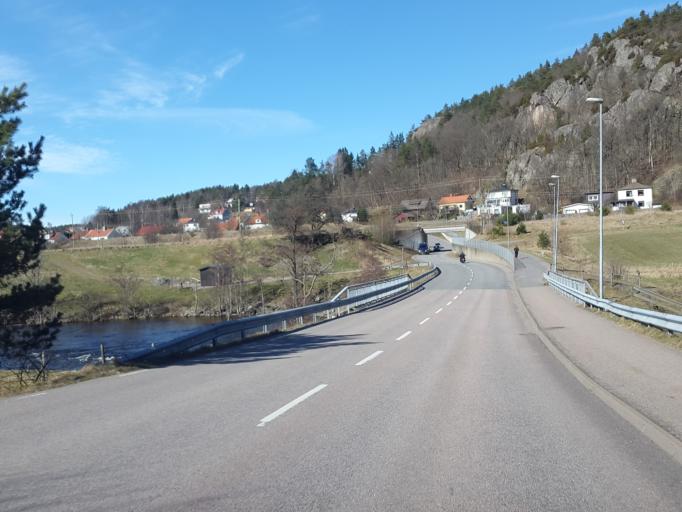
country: SE
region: Vaestra Goetaland
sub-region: Partille Kommun
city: Furulund
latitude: 57.7459
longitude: 12.1579
